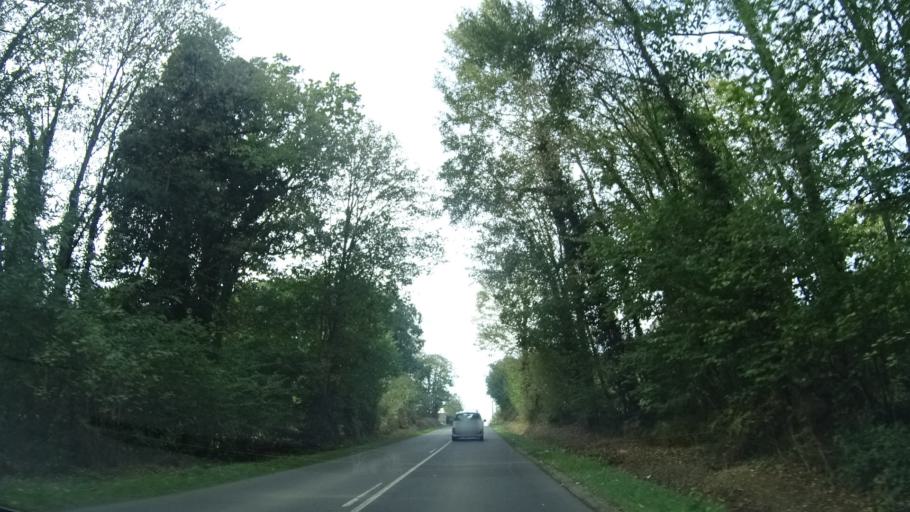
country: FR
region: Brittany
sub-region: Departement d'Ille-et-Vilaine
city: Meillac
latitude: 48.4310
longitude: -1.7880
